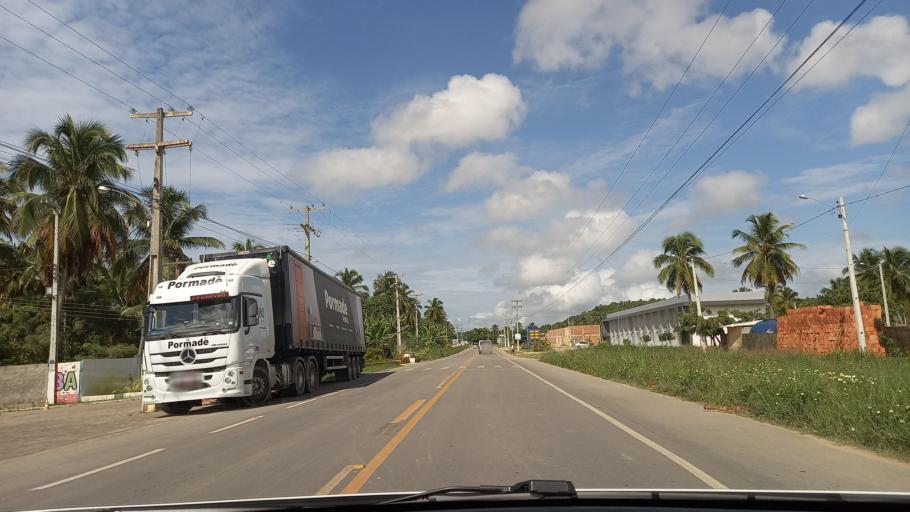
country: BR
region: Pernambuco
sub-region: Sao Jose Da Coroa Grande
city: Sao Jose da Coroa Grande
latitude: -8.9388
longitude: -35.1712
